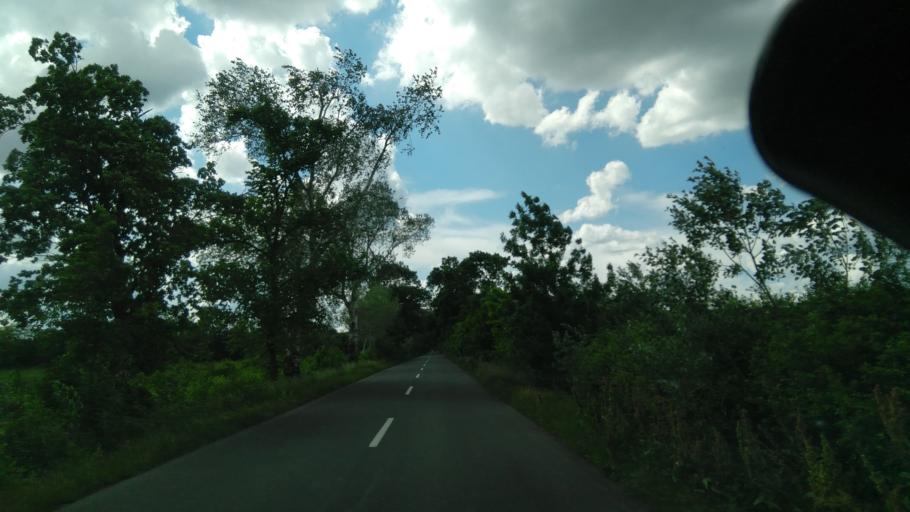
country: HU
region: Bekes
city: Bucsa
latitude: 47.1657
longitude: 21.0853
